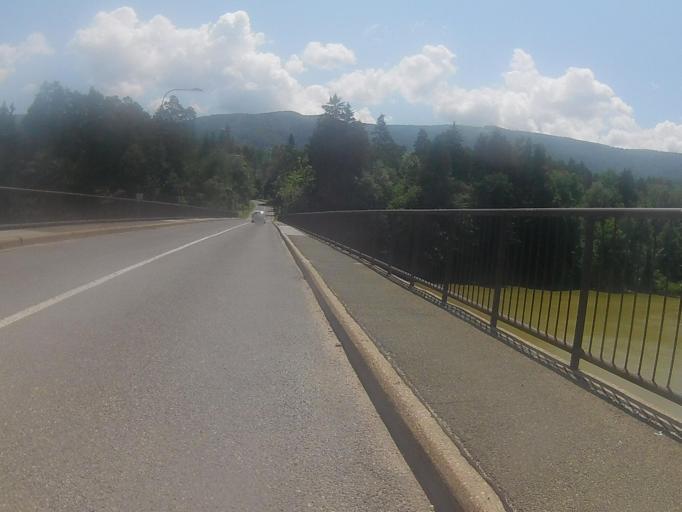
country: SI
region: Selnica ob Dravi
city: Selnica ob Dravi
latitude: 46.5439
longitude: 15.4997
